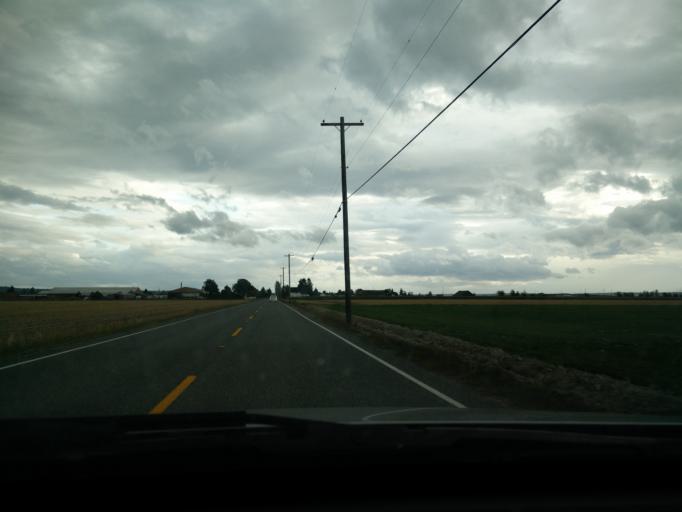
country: US
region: Washington
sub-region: Snohomish County
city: Stanwood
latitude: 48.2552
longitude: -122.3708
